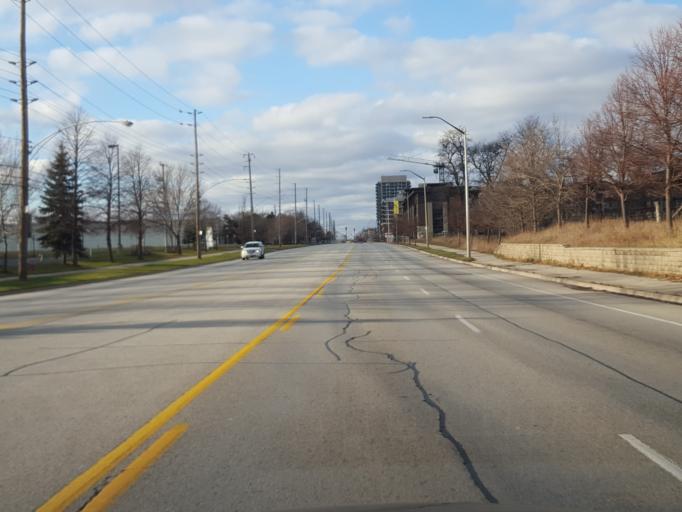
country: CA
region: Ontario
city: Burlington
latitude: 43.3880
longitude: -79.7822
